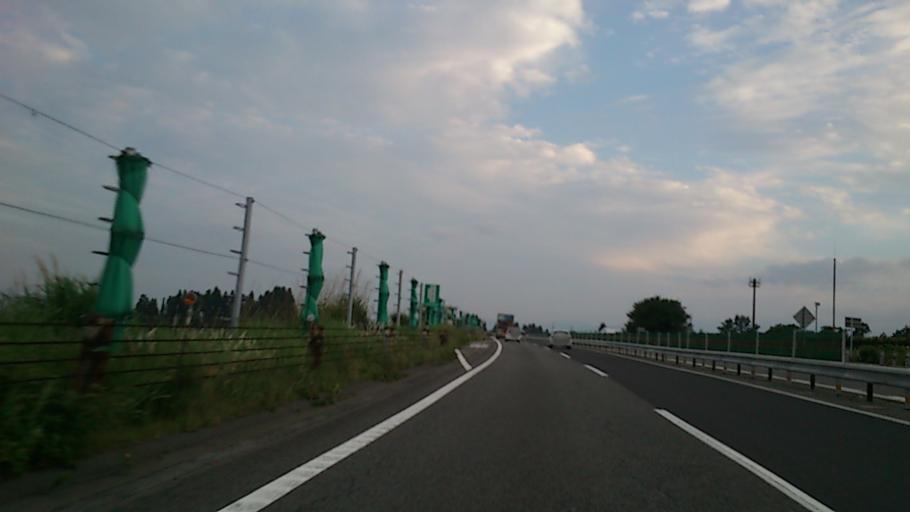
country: JP
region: Nagano
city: Iida
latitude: 35.5625
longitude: 137.8621
